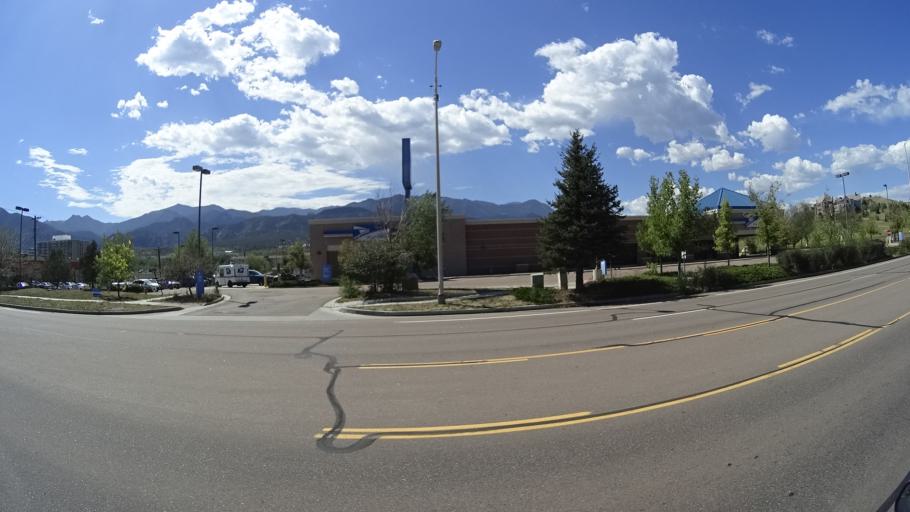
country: US
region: Colorado
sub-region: El Paso County
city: Colorado Springs
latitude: 38.8106
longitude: -104.8408
